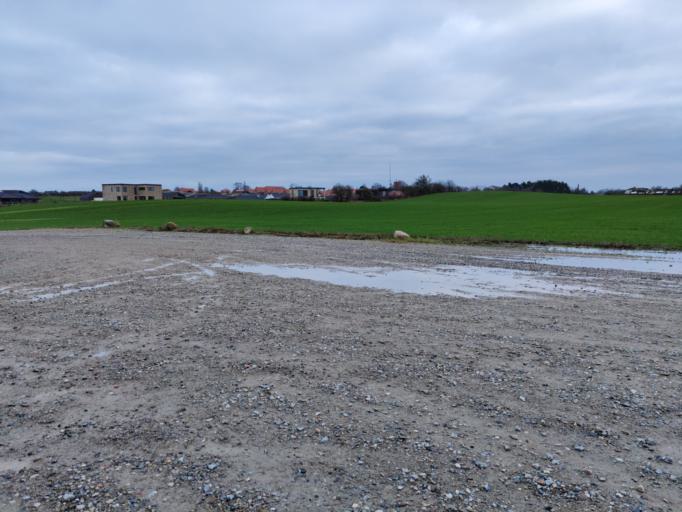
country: DK
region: South Denmark
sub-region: Kerteminde Kommune
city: Kerteminde
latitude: 55.4664
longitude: 10.6549
